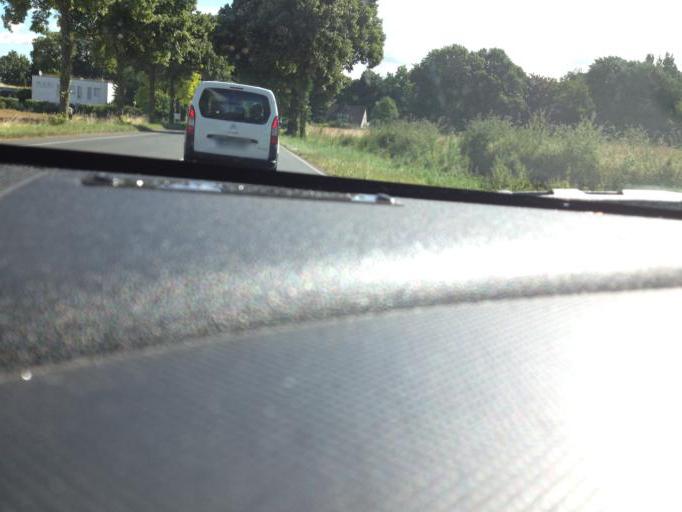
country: DE
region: North Rhine-Westphalia
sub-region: Regierungsbezirk Arnsberg
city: Holzwickede
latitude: 51.5252
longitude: 7.6488
